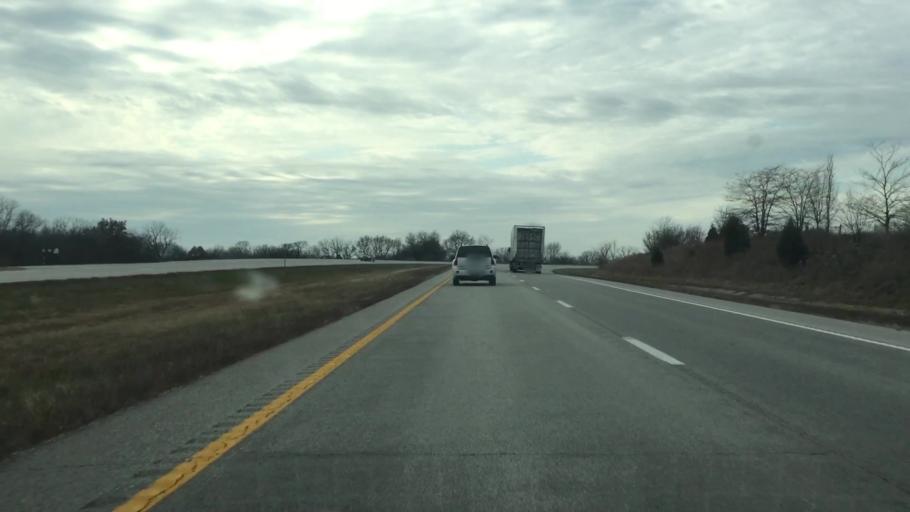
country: US
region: Missouri
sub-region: Cass County
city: Garden City
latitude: 38.5180
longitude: -94.1355
